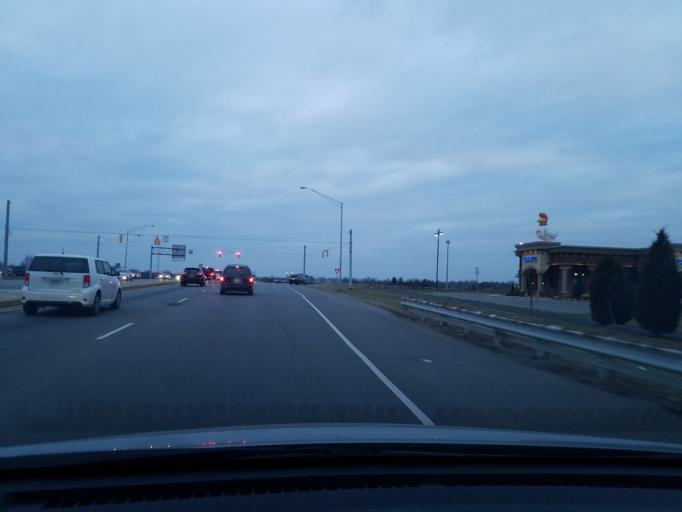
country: US
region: Indiana
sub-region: Clark County
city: Clarksville
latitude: 38.3415
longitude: -85.7994
